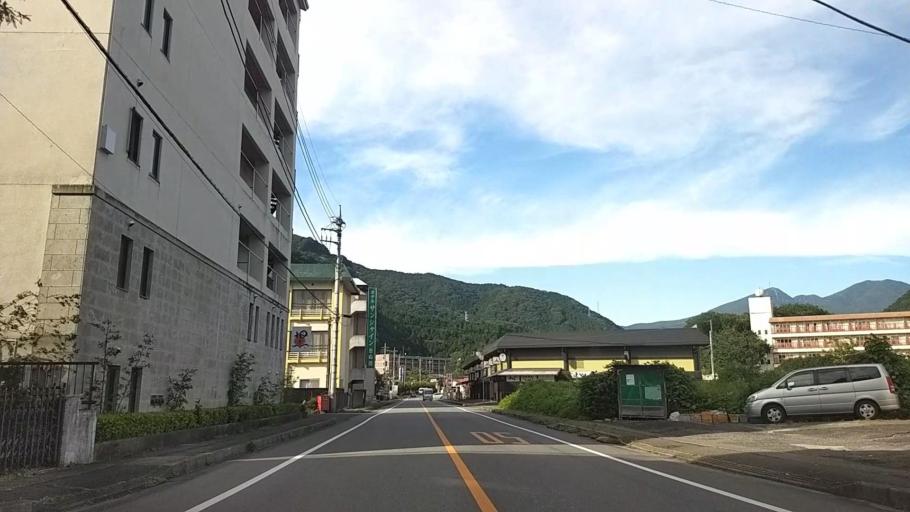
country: JP
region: Tochigi
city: Imaichi
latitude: 36.8194
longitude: 139.7100
